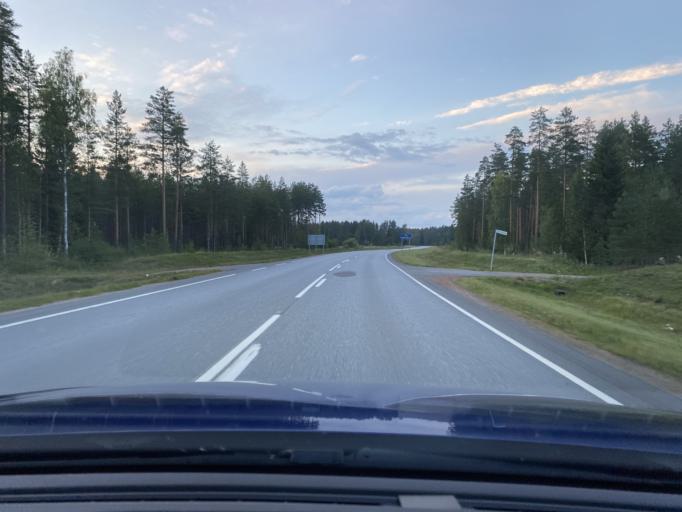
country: FI
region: Satakunta
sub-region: Pohjois-Satakunta
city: Honkajoki
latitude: 62.0176
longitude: 22.2257
